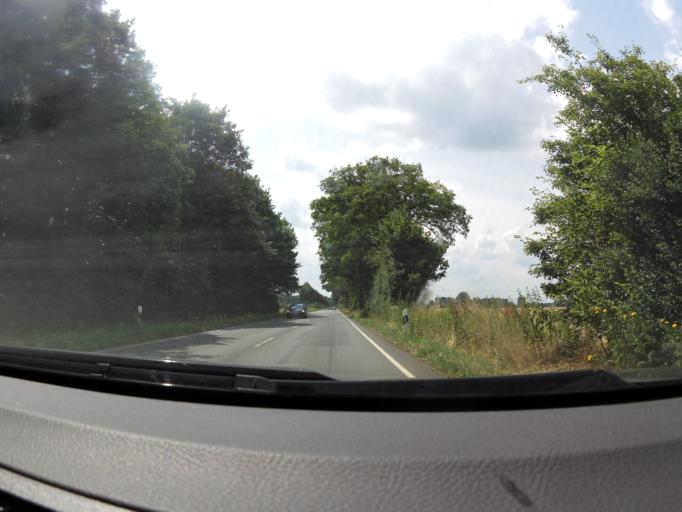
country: DE
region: North Rhine-Westphalia
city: Geldern
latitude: 51.5516
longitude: 6.3277
